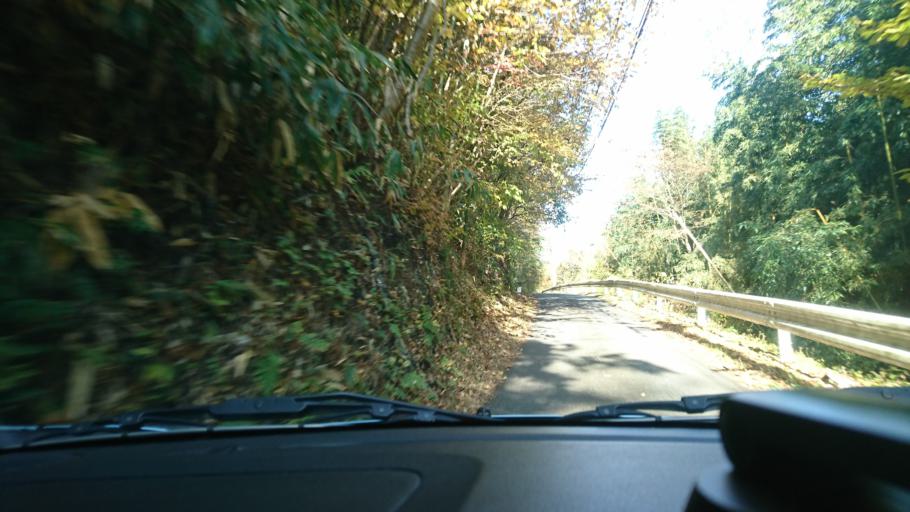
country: JP
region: Iwate
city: Ichinoseki
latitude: 38.7981
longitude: 141.2463
